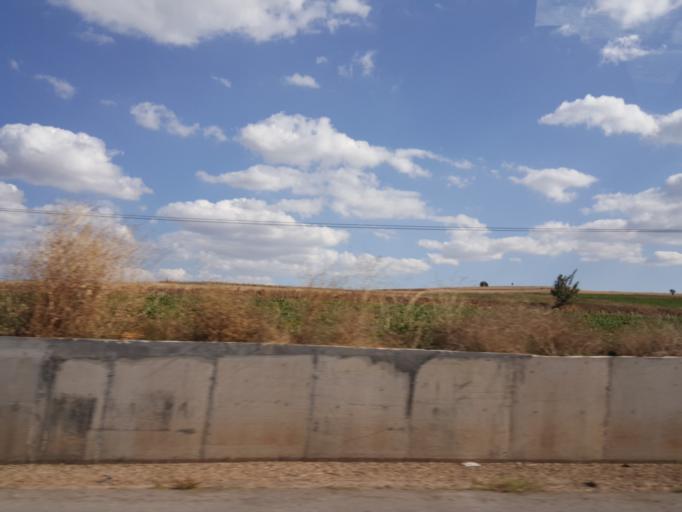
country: TR
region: Tokat
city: Sulusaray
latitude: 39.9830
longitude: 36.0669
